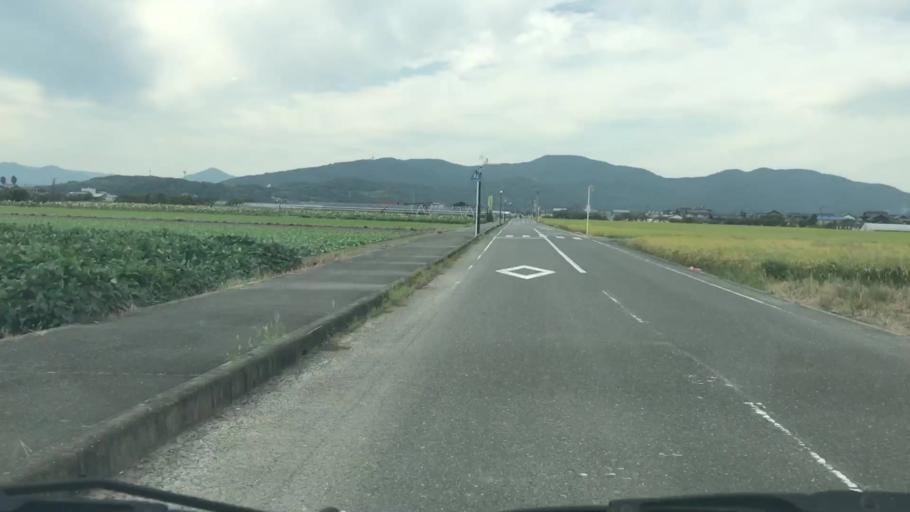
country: JP
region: Saga Prefecture
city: Kashima
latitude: 33.1454
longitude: 130.1416
